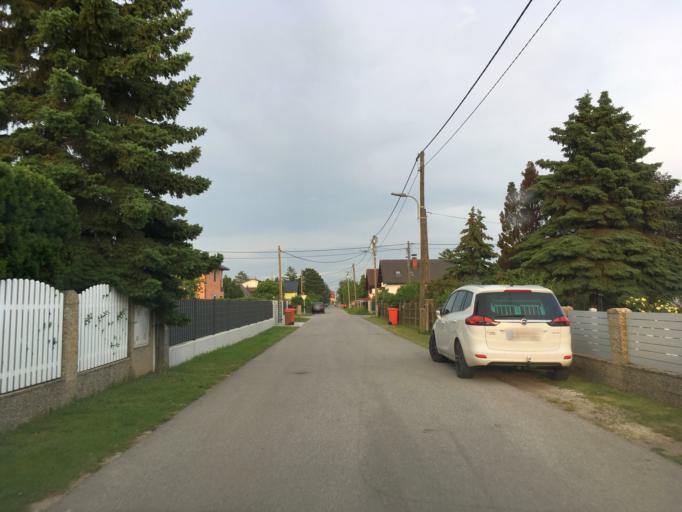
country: AT
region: Lower Austria
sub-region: Politischer Bezirk Wien-Umgebung
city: Gerasdorf bei Wien
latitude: 48.3176
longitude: 16.4983
